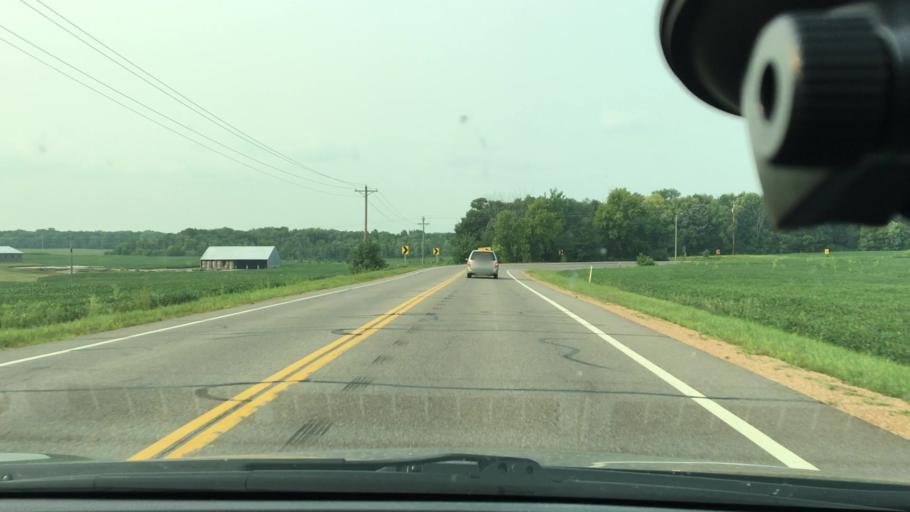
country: US
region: Minnesota
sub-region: Hennepin County
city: Champlin
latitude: 45.1868
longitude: -93.4624
